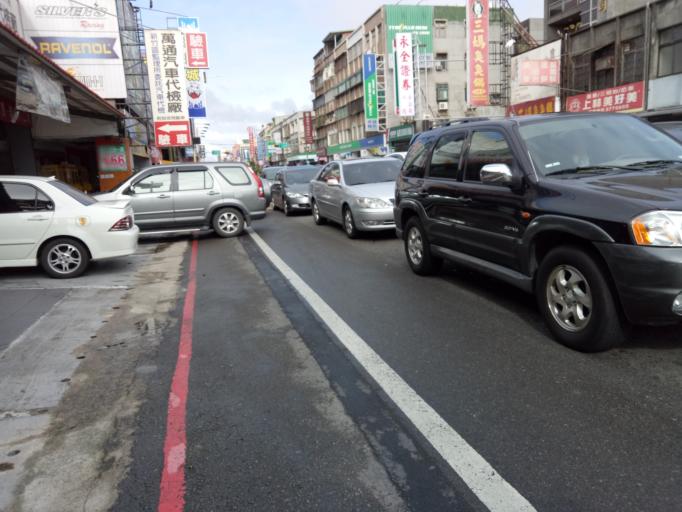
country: TW
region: Taiwan
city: Taoyuan City
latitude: 24.9661
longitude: 121.3008
